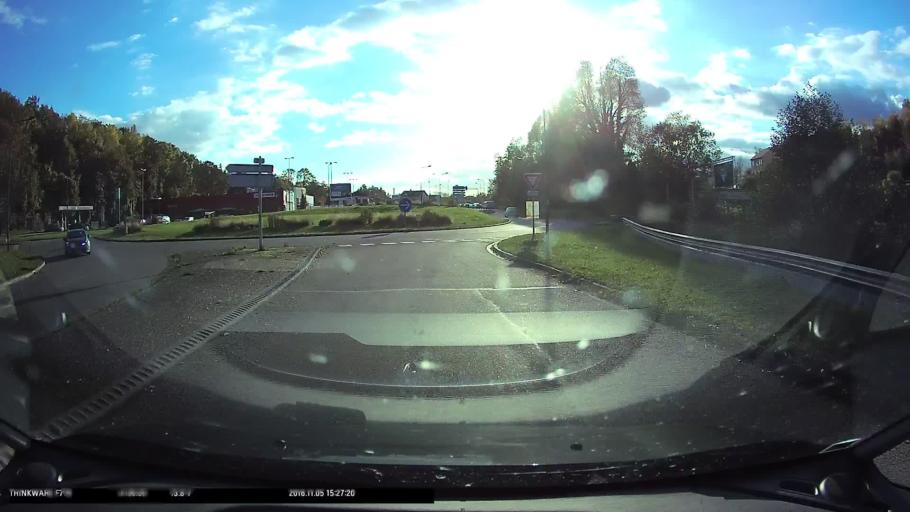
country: FR
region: Ile-de-France
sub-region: Departement des Yvelines
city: Meulan-en-Yvelines
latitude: 49.0135
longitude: 1.9090
